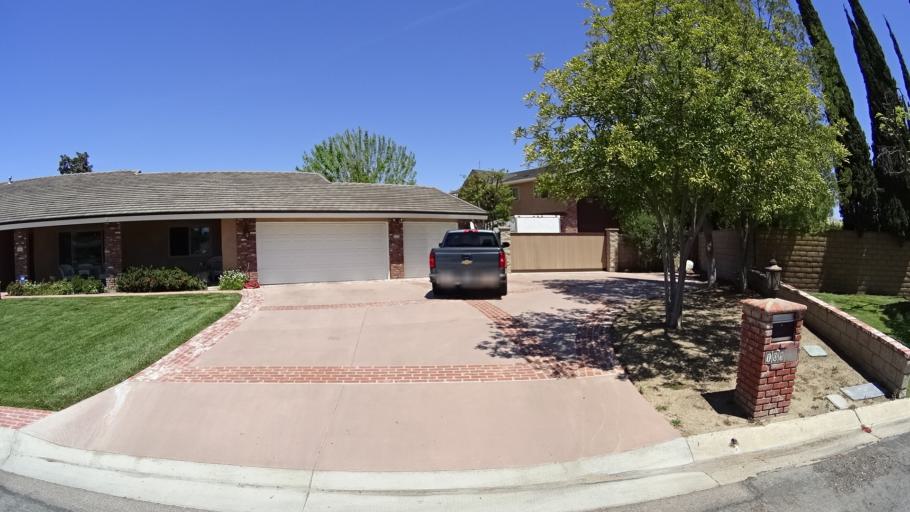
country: US
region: California
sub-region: Orange County
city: Villa Park
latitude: 33.8093
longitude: -117.8168
